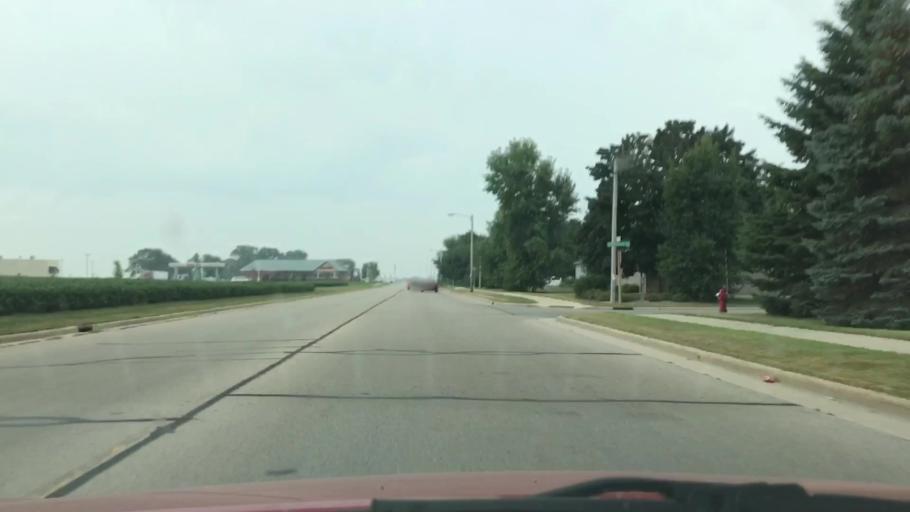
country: US
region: Wisconsin
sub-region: Outagamie County
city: Seymour
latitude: 44.5041
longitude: -88.3205
